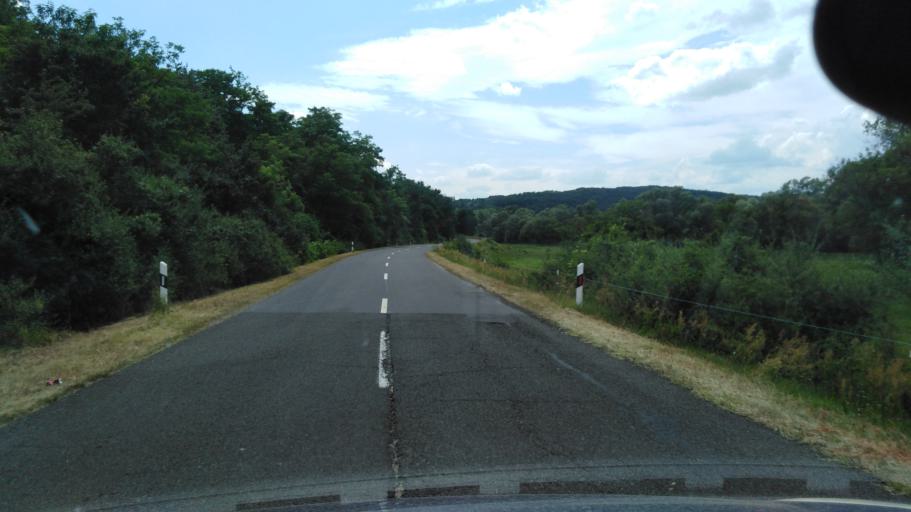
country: HU
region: Nograd
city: Szecseny
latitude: 48.2040
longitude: 19.5299
